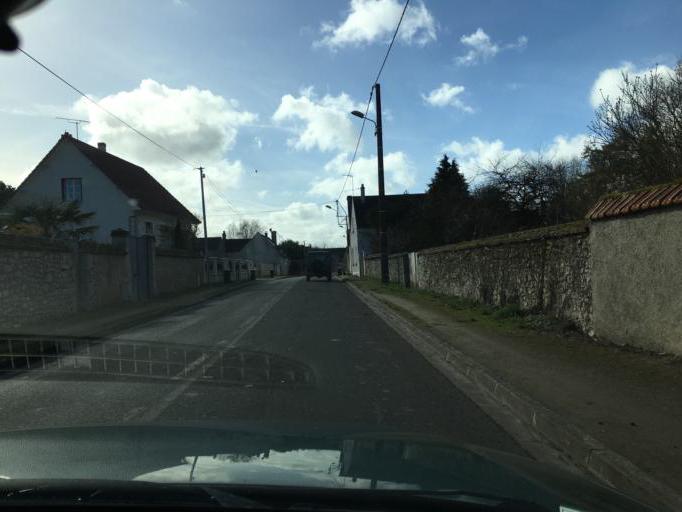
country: FR
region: Centre
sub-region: Departement du Loiret
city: Meung-sur-Loire
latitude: 47.8544
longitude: 1.7052
